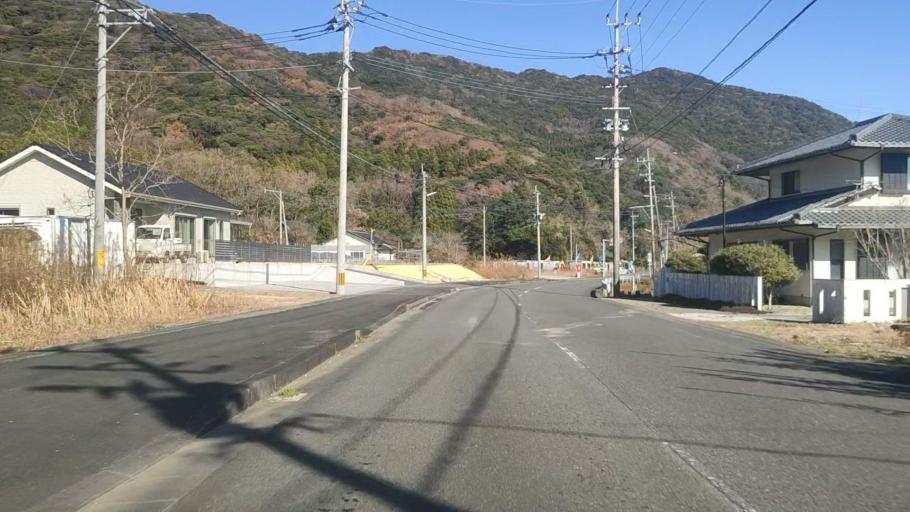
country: JP
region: Oita
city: Saiki
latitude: 32.8049
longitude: 131.9450
